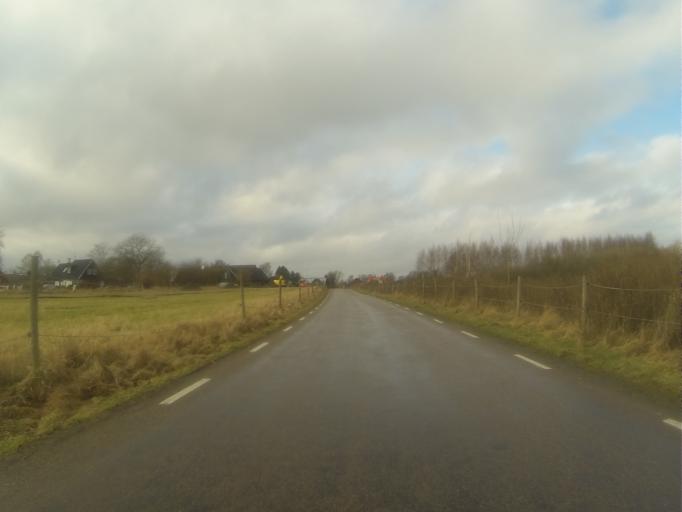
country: SE
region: Skane
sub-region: Svedala Kommun
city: Klagerup
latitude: 55.5690
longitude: 13.3079
